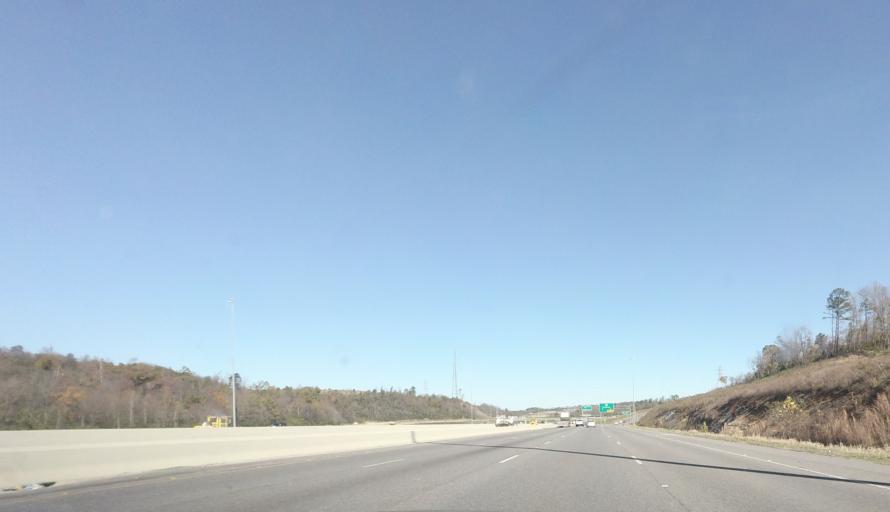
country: US
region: Alabama
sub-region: Jefferson County
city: Fultondale
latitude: 33.5798
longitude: -86.8103
